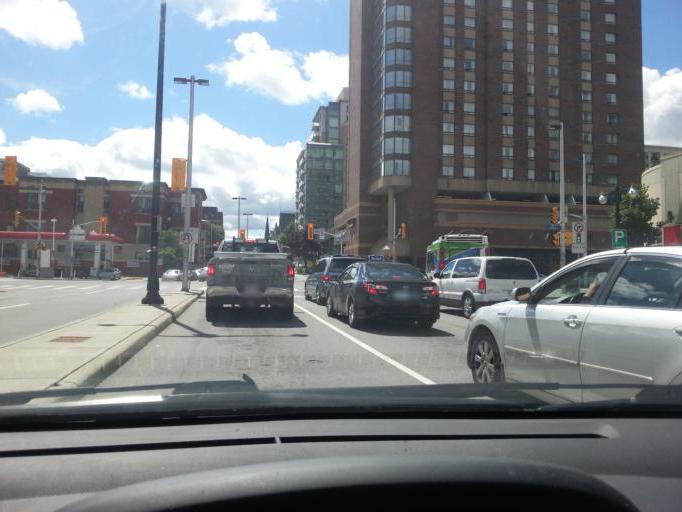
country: CA
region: Ontario
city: Ottawa
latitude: 45.4291
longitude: -75.6861
